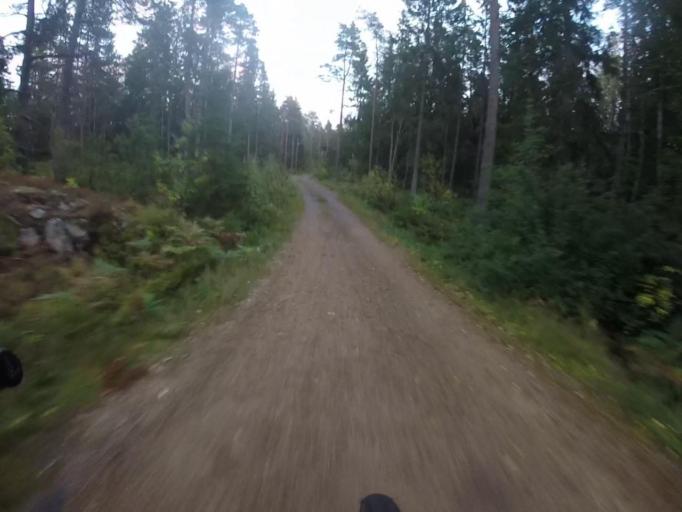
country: SE
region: Vaestra Goetaland
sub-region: Trollhattan
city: Trollhattan
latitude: 58.2948
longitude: 12.2571
